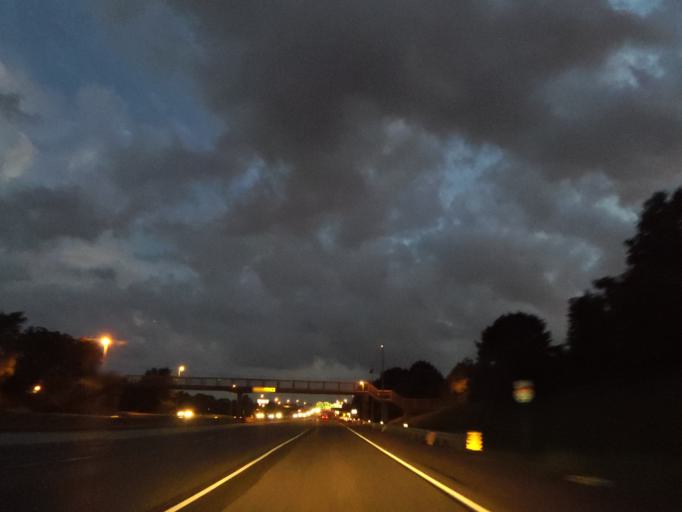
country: US
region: Missouri
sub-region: Saint Louis County
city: Saint George
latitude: 38.5368
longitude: -90.3080
